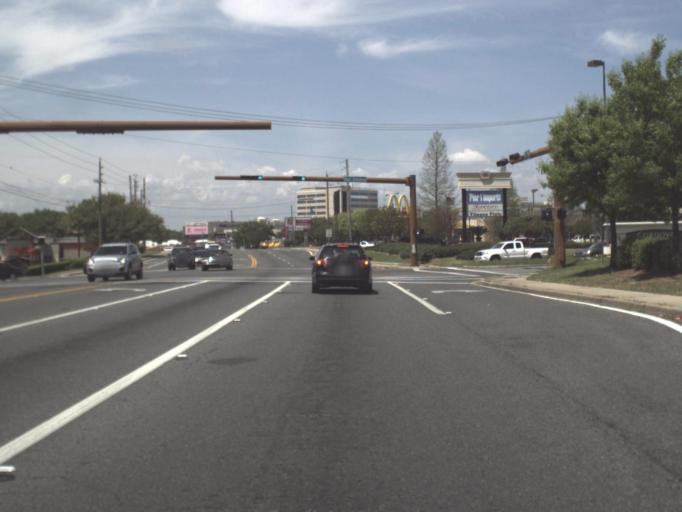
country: US
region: Florida
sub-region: Escambia County
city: Brent
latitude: 30.4705
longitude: -87.2074
